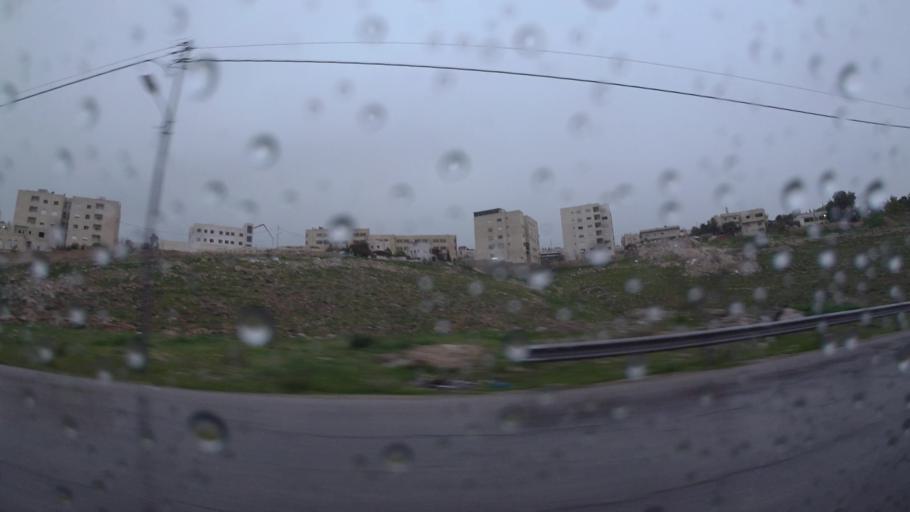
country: JO
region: Amman
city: Amman
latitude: 31.9977
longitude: 35.9693
